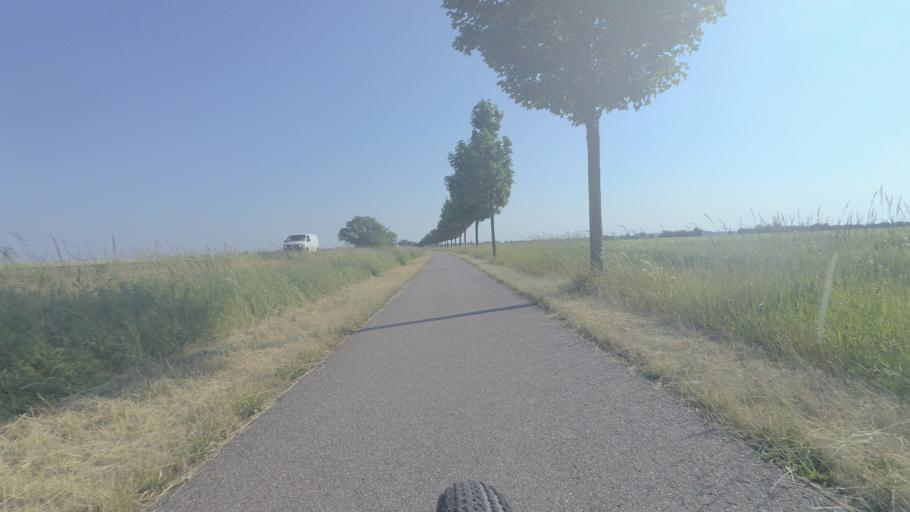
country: DE
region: Saxony-Anhalt
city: Osternienburger Land
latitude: 51.7825
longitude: 12.0061
